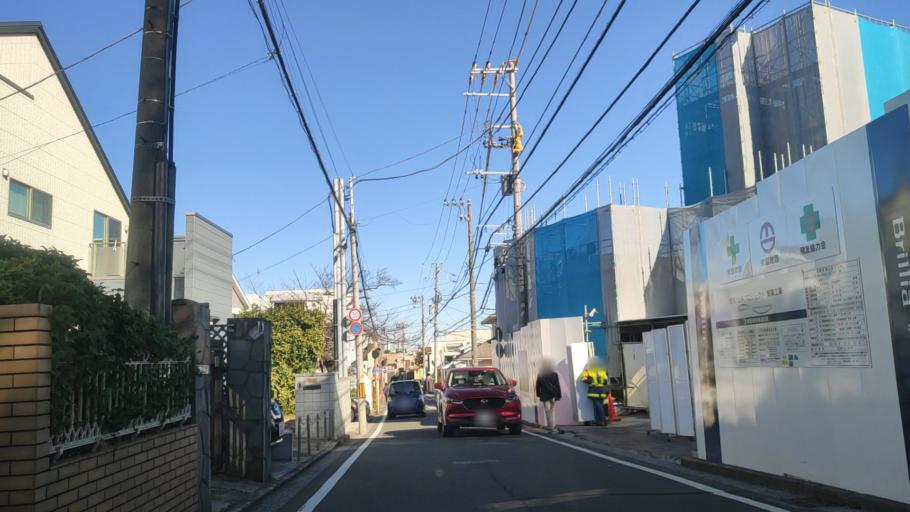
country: JP
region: Kanagawa
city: Yokohama
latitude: 35.4295
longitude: 139.6442
